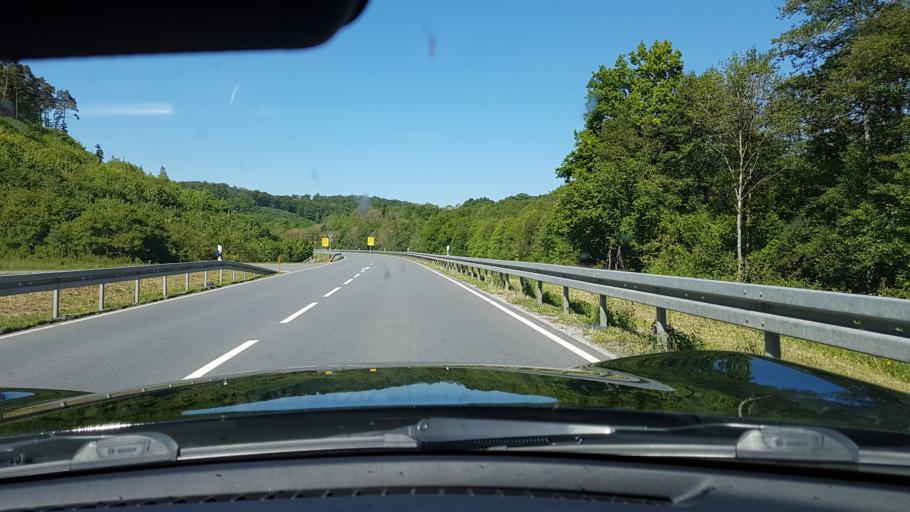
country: DE
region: Baden-Wuerttemberg
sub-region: Karlsruhe Region
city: Adelsheim
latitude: 49.4214
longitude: 9.3988
